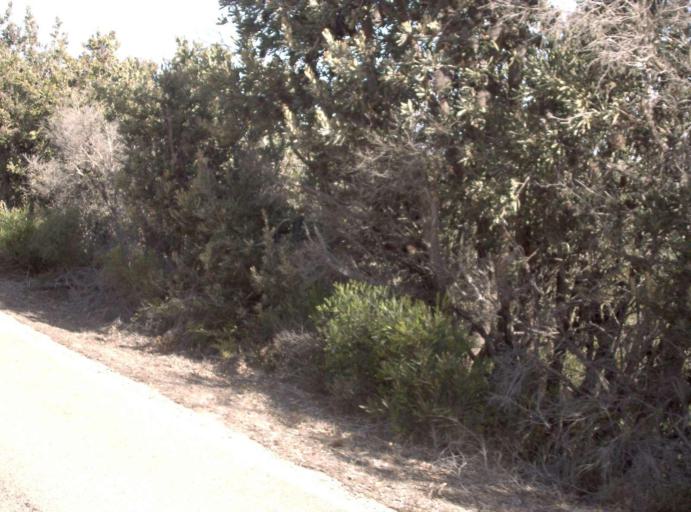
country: AU
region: Victoria
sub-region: East Gippsland
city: Lakes Entrance
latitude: -37.7975
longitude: 148.7098
